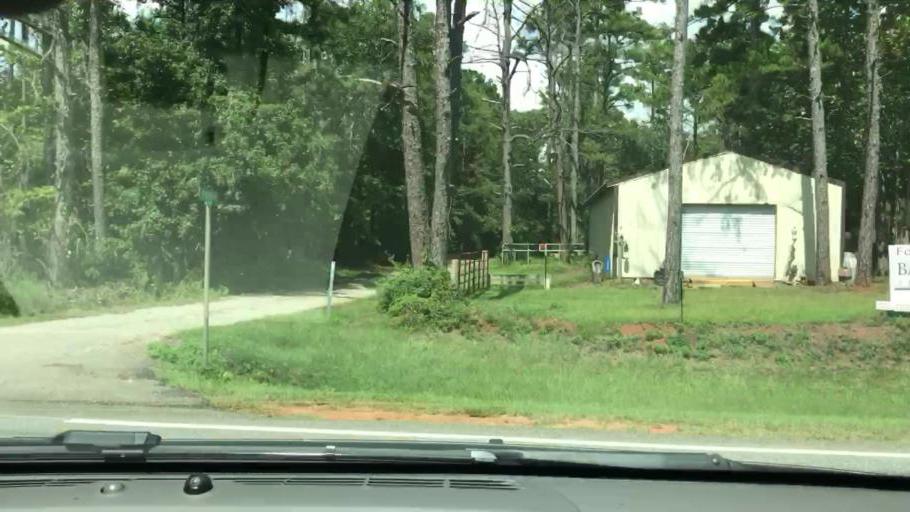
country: US
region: Georgia
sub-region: Quitman County
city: Georgetown
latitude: 31.8602
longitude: -85.0680
